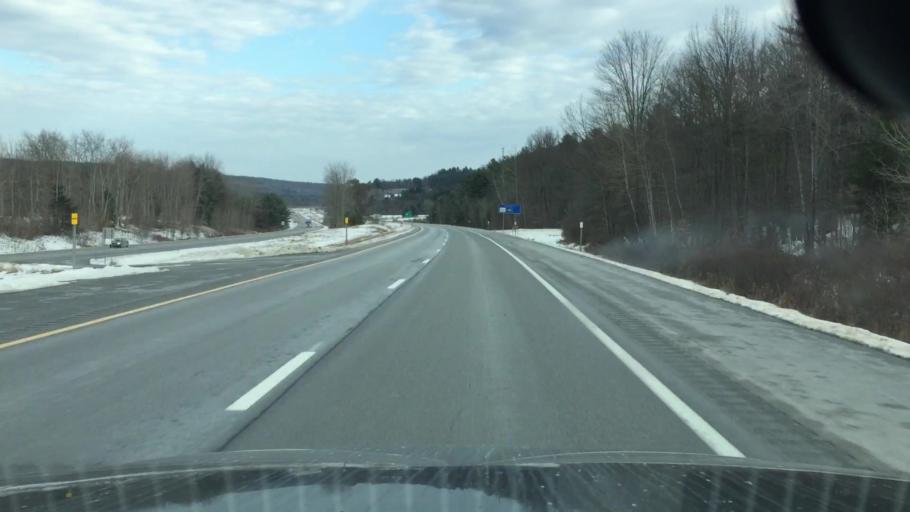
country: US
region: New York
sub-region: Chenango County
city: Bainbridge
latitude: 42.2109
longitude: -75.5167
